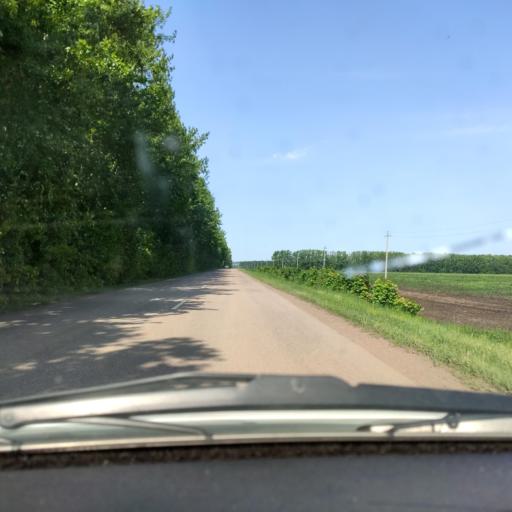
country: RU
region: Bashkortostan
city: Avdon
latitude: 54.5074
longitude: 55.6220
